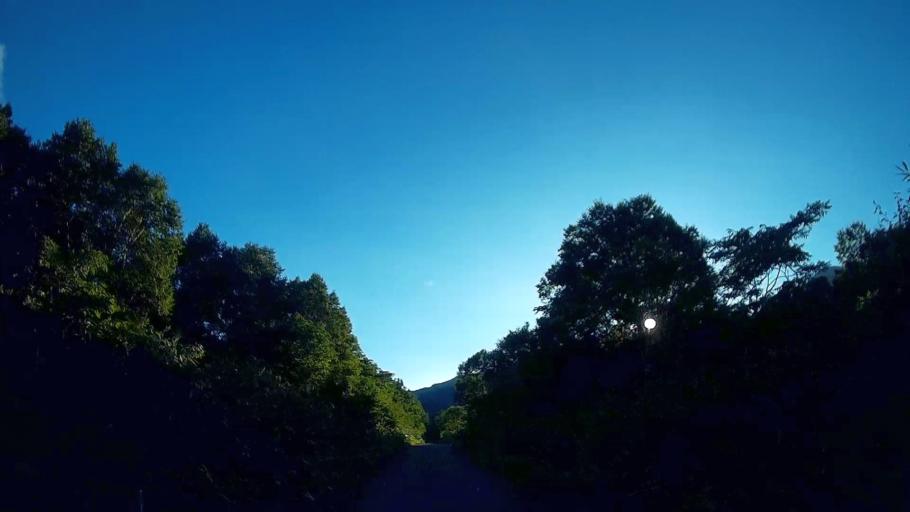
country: JP
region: Hokkaido
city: Iwanai
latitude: 42.6053
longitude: 139.9990
